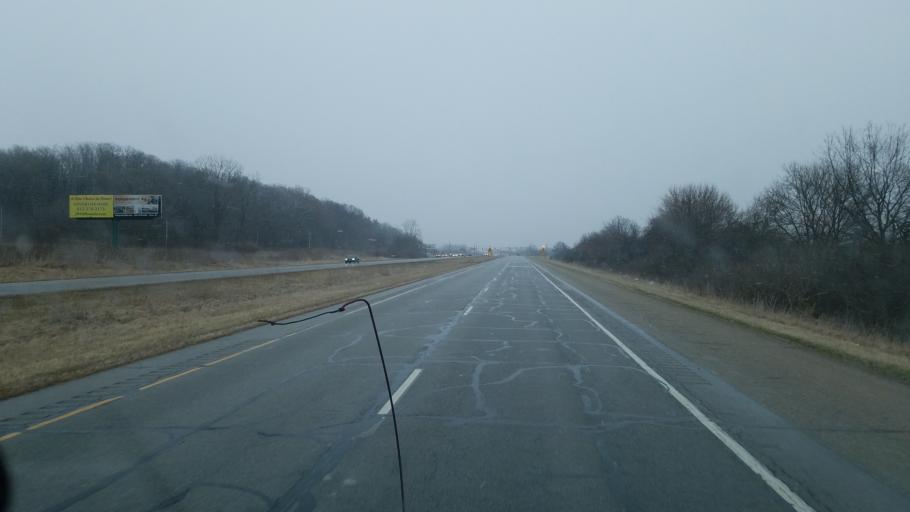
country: US
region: Indiana
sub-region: Miami County
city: Peru
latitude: 40.7733
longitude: -86.0893
